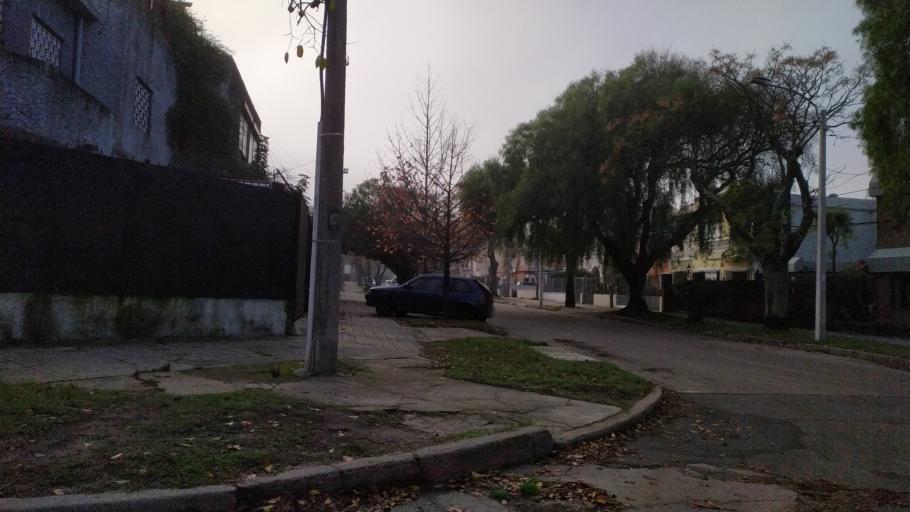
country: UY
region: Canelones
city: Paso de Carrasco
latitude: -34.8931
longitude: -56.0986
